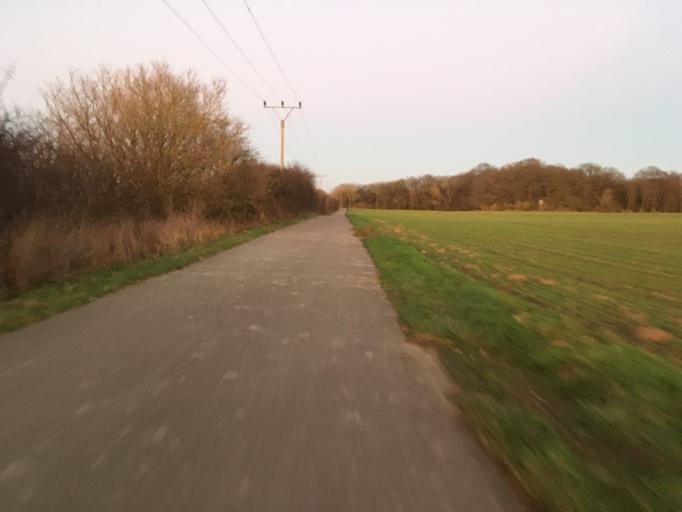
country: DE
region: Mecklenburg-Vorpommern
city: Ostseebad Binz
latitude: 54.3826
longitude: 13.5974
